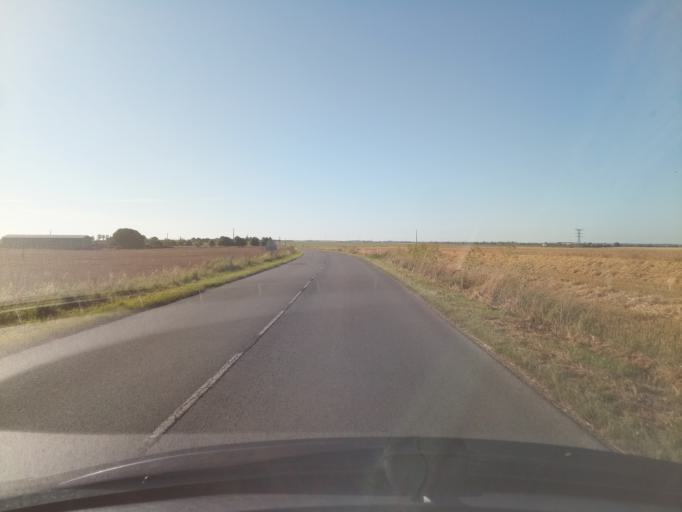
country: FR
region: Poitou-Charentes
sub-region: Departement de la Charente-Maritime
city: Marans
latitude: 46.3002
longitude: -0.9807
